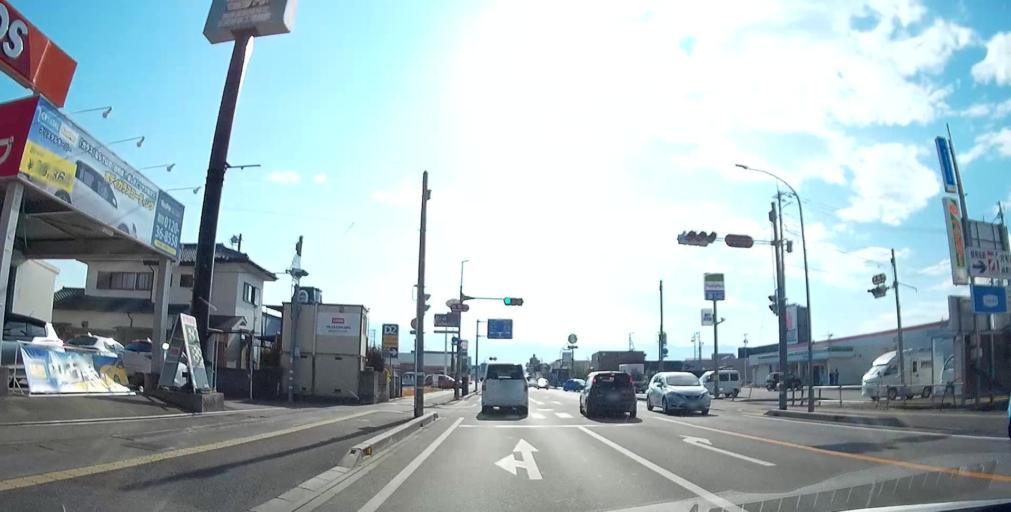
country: JP
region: Yamanashi
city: Isawa
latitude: 35.6494
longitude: 138.6130
